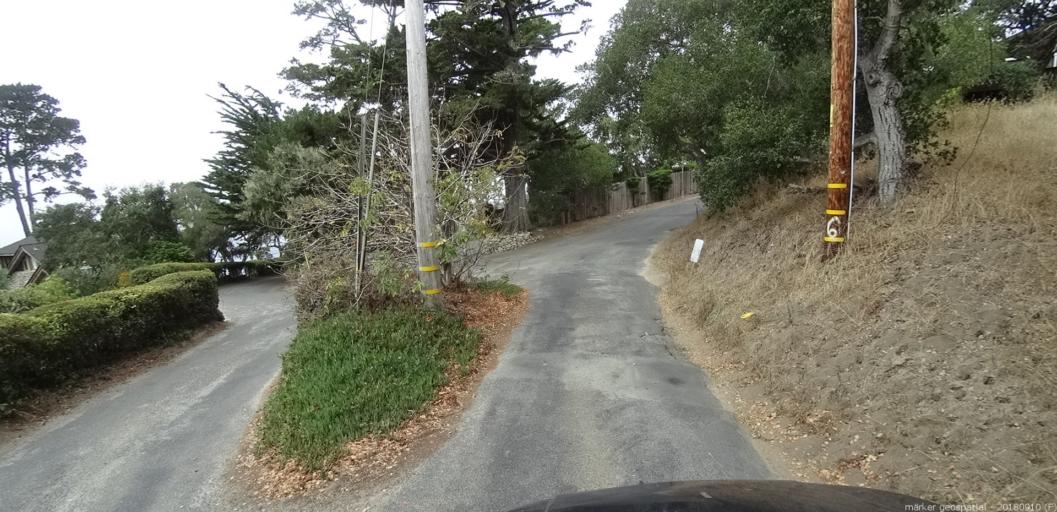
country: US
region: California
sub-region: Monterey County
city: Carmel-by-the-Sea
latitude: 36.4992
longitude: -121.9329
